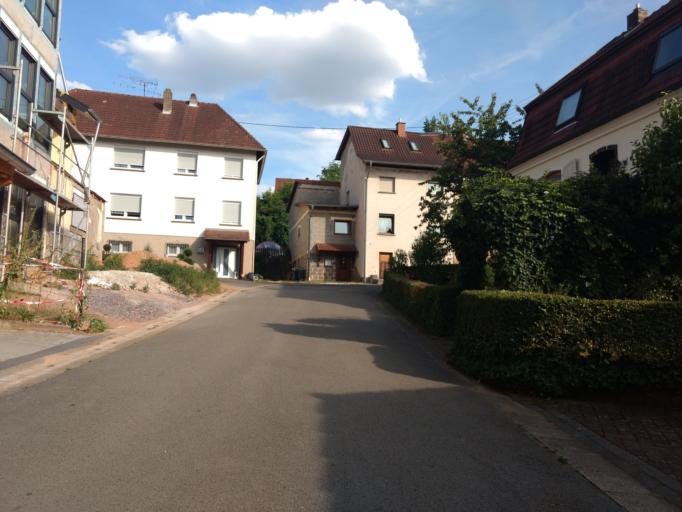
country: DE
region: Saarland
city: Beckingen
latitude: 49.3920
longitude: 6.7050
